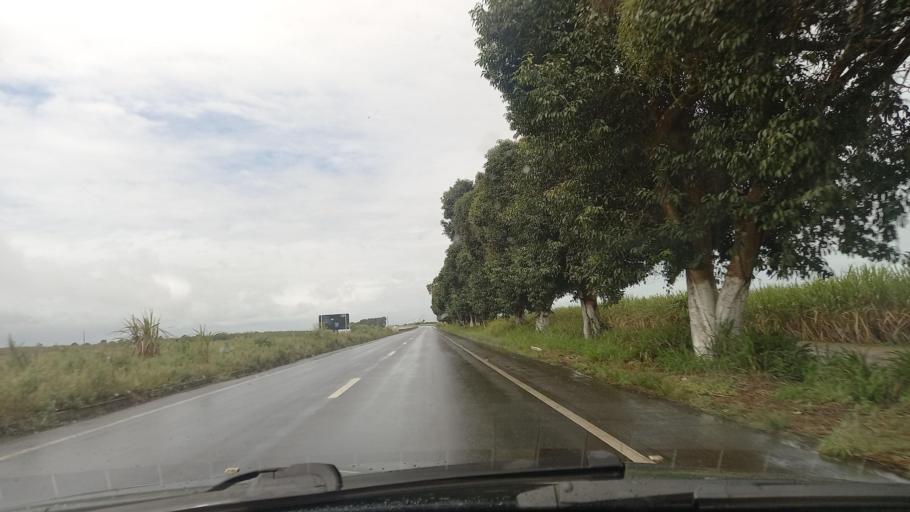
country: BR
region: Alagoas
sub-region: Campo Alegre
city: Campo Alegre
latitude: -9.7998
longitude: -36.2900
